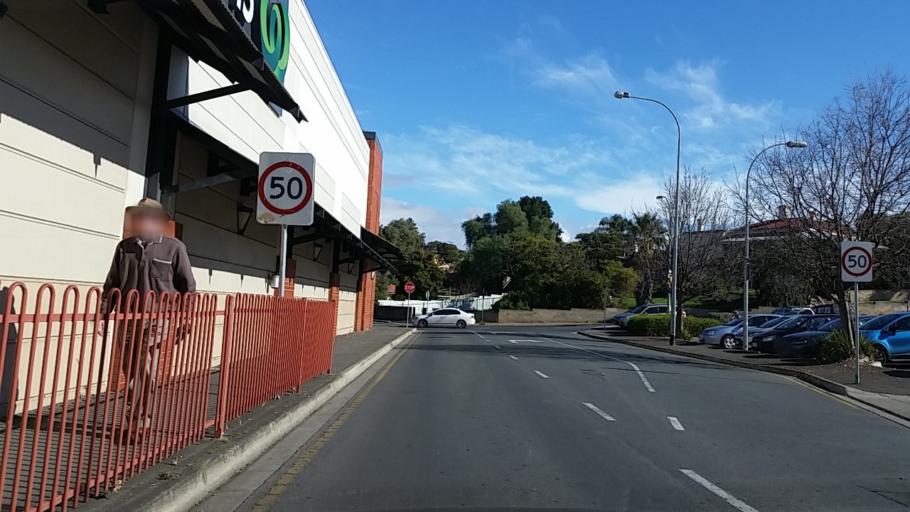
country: AU
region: South Australia
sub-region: Gawler
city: Gawler
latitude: -34.5969
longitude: 138.7479
